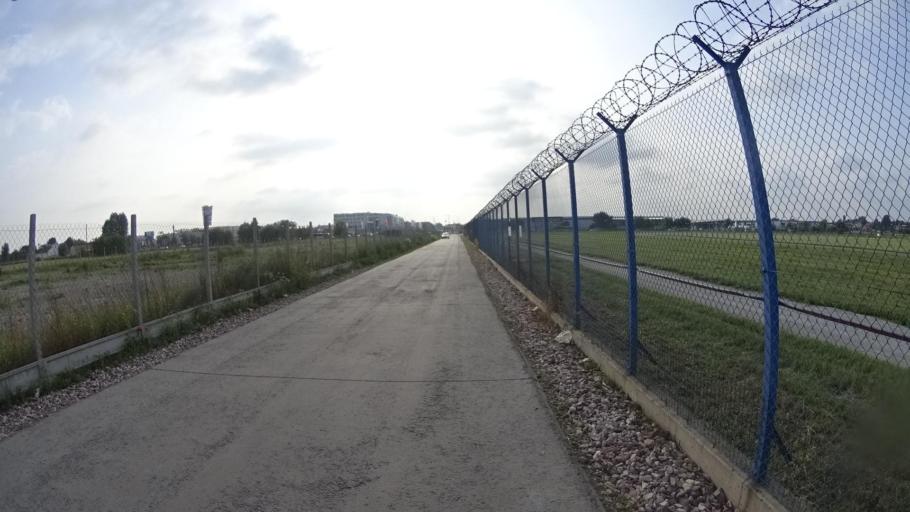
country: PL
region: Masovian Voivodeship
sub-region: Warszawa
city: Wlochy
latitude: 52.1711
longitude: 20.9422
